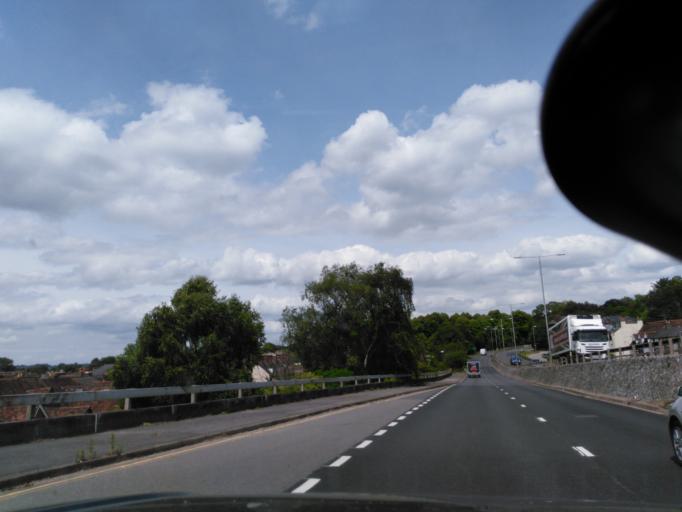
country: GB
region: England
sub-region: Wiltshire
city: Salisbury
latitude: 51.0687
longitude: -1.7899
